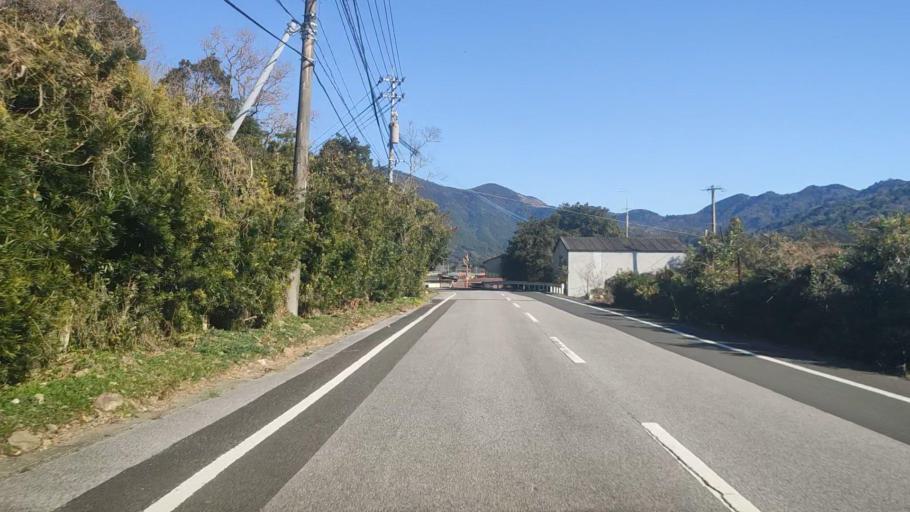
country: JP
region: Oita
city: Saiki
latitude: 32.7998
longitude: 131.8880
